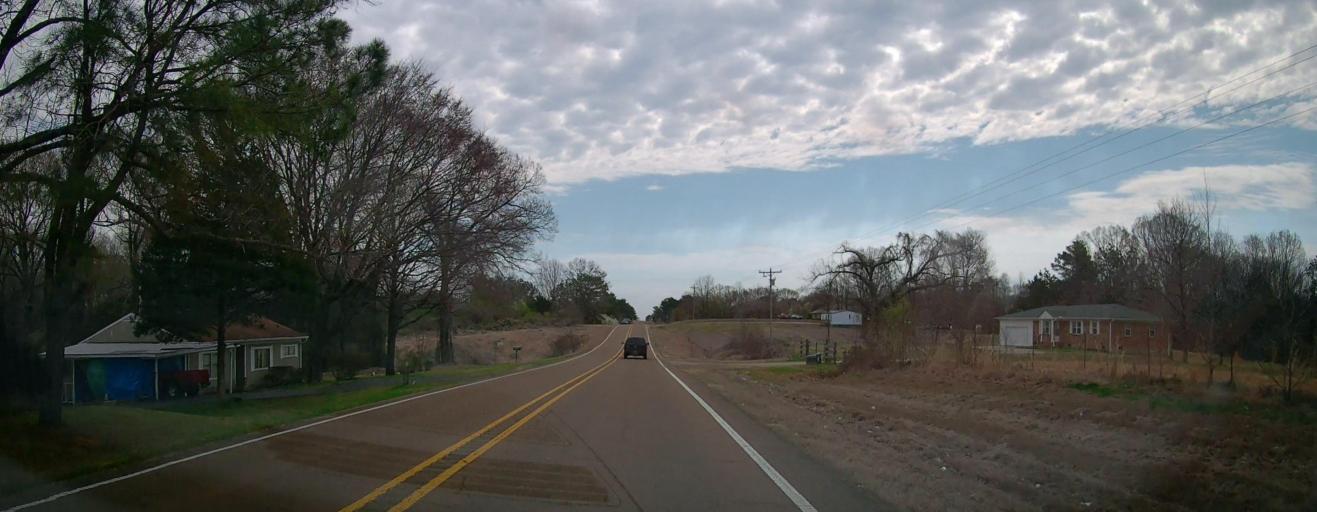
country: US
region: Mississippi
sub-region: Marshall County
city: Byhalia
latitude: 34.8431
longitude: -89.6086
